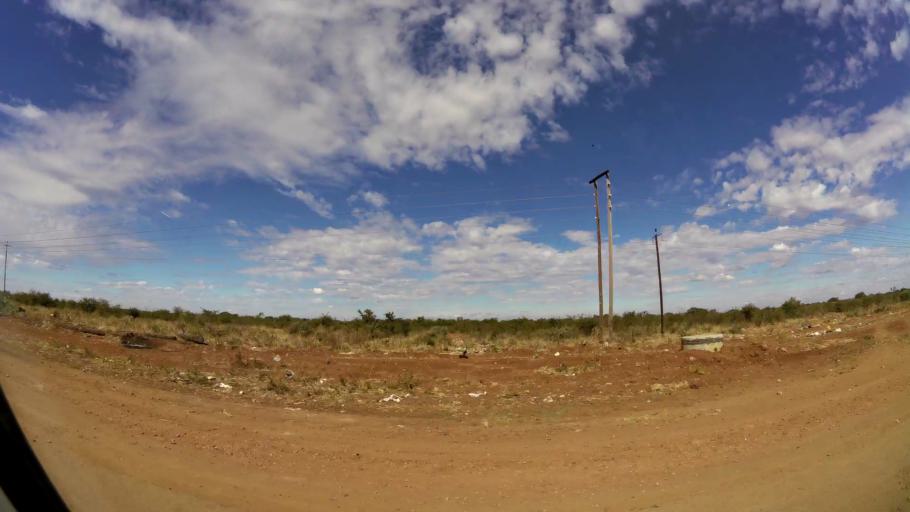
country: ZA
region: Limpopo
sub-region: Waterberg District Municipality
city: Bela-Bela
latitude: -24.8921
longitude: 28.3192
